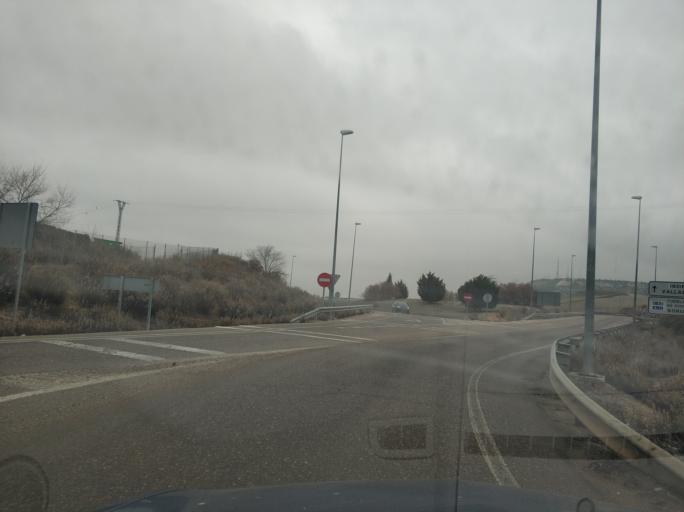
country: ES
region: Castille and Leon
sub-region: Provincia de Valladolid
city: Cisterniga
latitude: 41.6151
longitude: -4.6866
